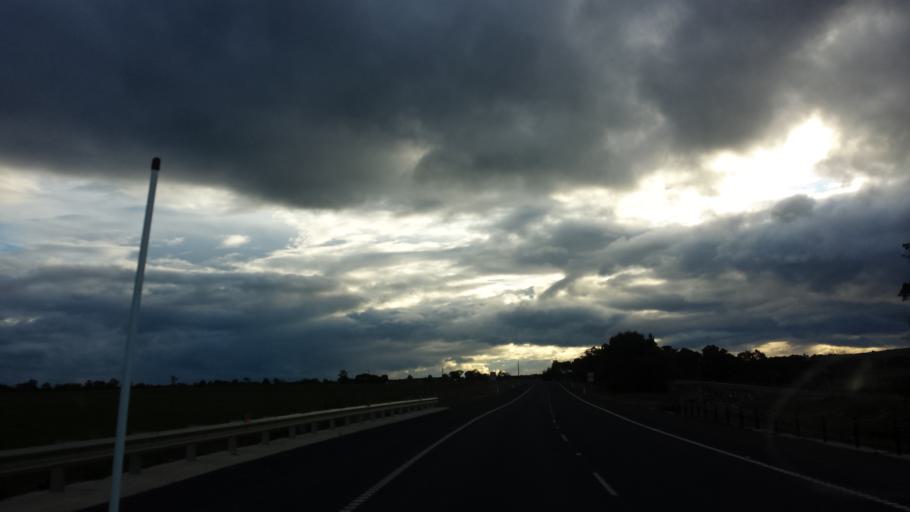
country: AU
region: Victoria
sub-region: Wellington
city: Heyfield
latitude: -38.1321
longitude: 146.8194
